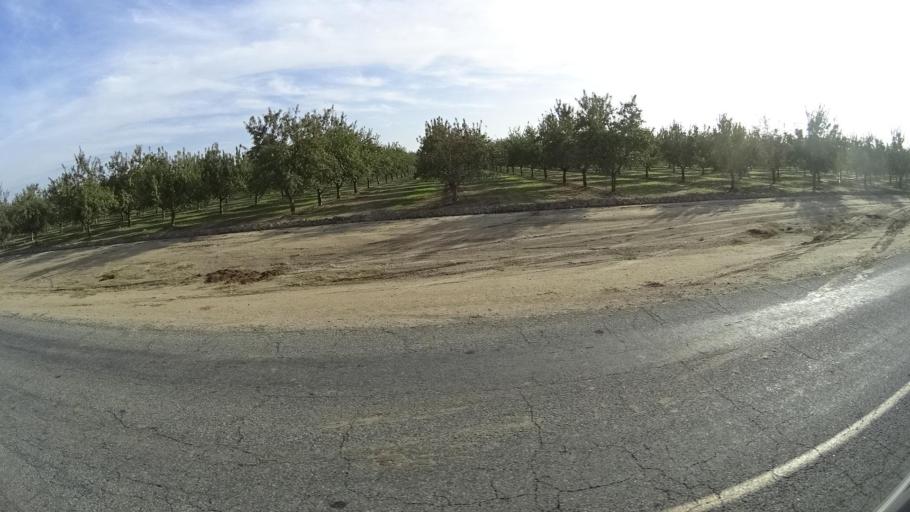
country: US
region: California
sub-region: Kern County
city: McFarland
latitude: 35.6883
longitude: -119.2048
